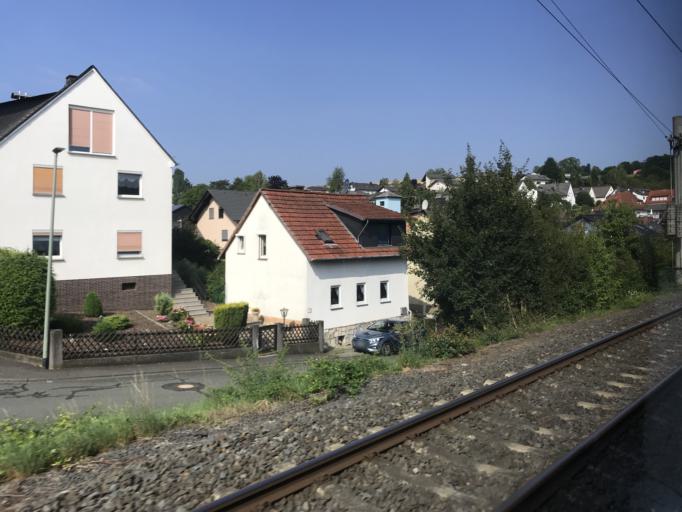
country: DE
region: Hesse
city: Bad Camberg
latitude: 50.3208
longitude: 8.2442
